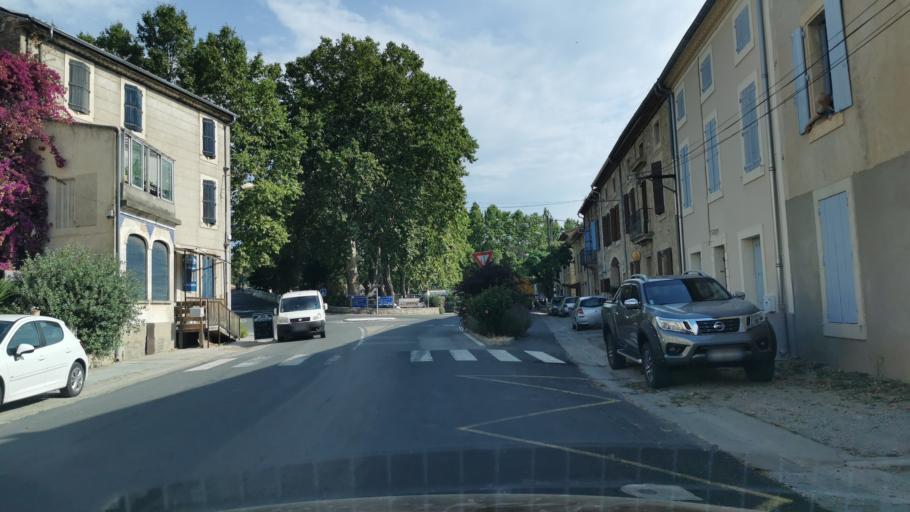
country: FR
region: Languedoc-Roussillon
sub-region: Departement de l'Aude
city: Bize-Minervois
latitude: 43.3155
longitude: 2.8706
